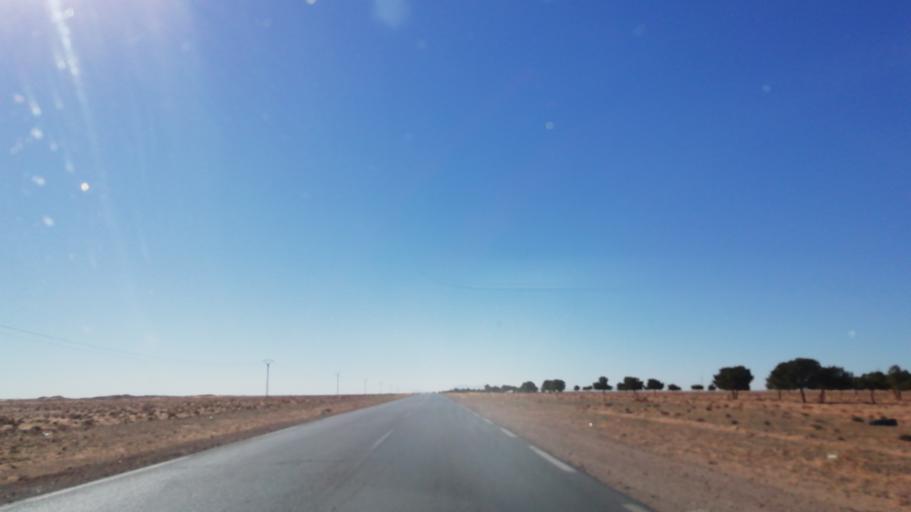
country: DZ
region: Saida
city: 'Ain el Hadjar
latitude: 33.9812
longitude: 0.0286
